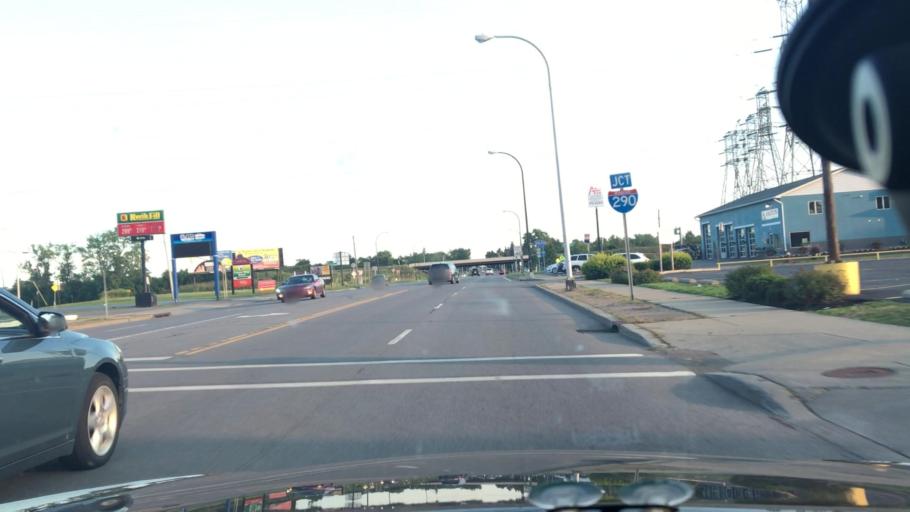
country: US
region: New York
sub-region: Erie County
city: Tonawanda
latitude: 42.9991
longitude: -78.8750
